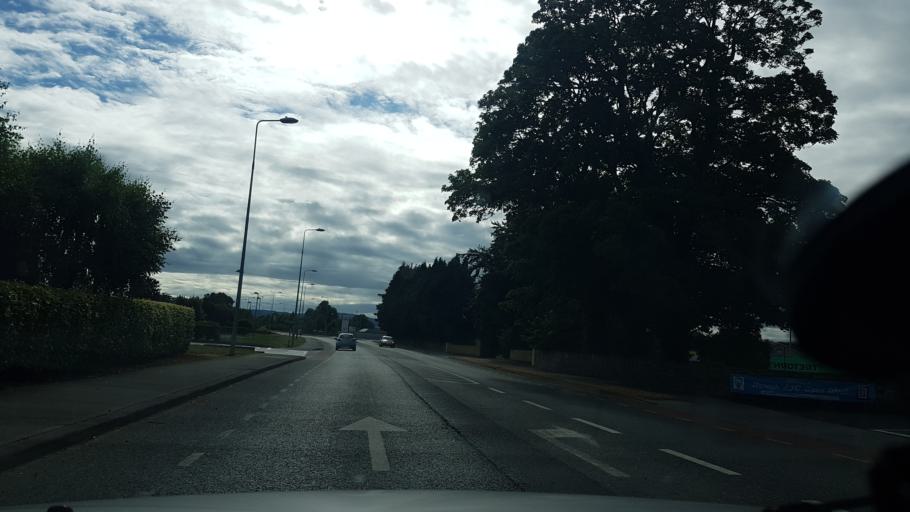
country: IE
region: Munster
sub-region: North Tipperary
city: Nenagh
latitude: 52.8614
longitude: -8.2133
